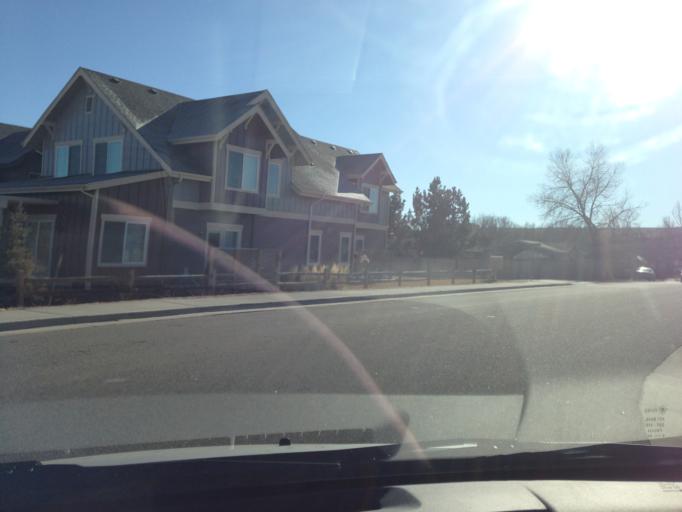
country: US
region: Colorado
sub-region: Boulder County
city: Superior
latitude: 39.9550
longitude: -105.1708
